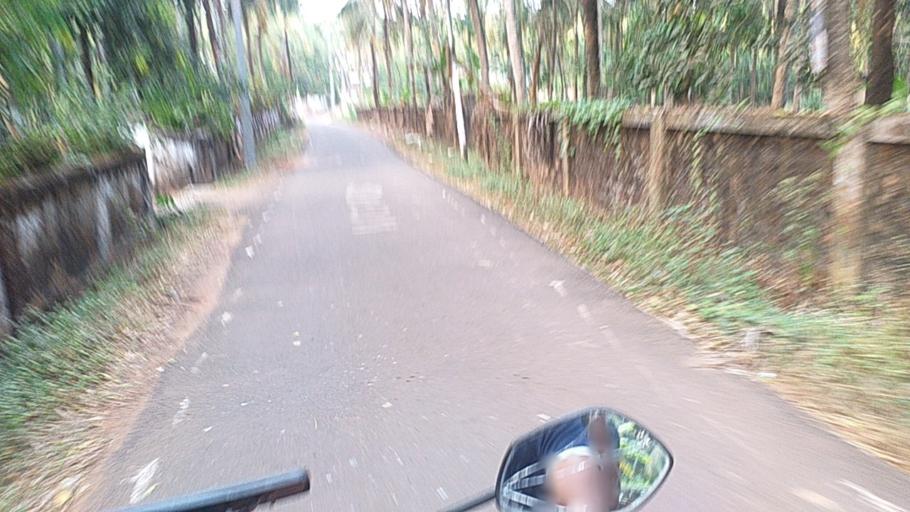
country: IN
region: Kerala
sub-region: Thrissur District
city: Kunnamkulam
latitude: 10.7342
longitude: 76.0448
